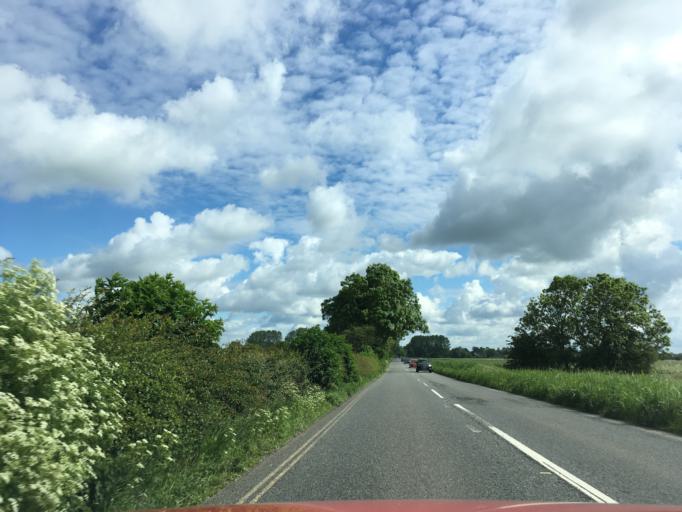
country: GB
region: England
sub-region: Gloucestershire
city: Lechlade
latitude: 51.6836
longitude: -1.7004
